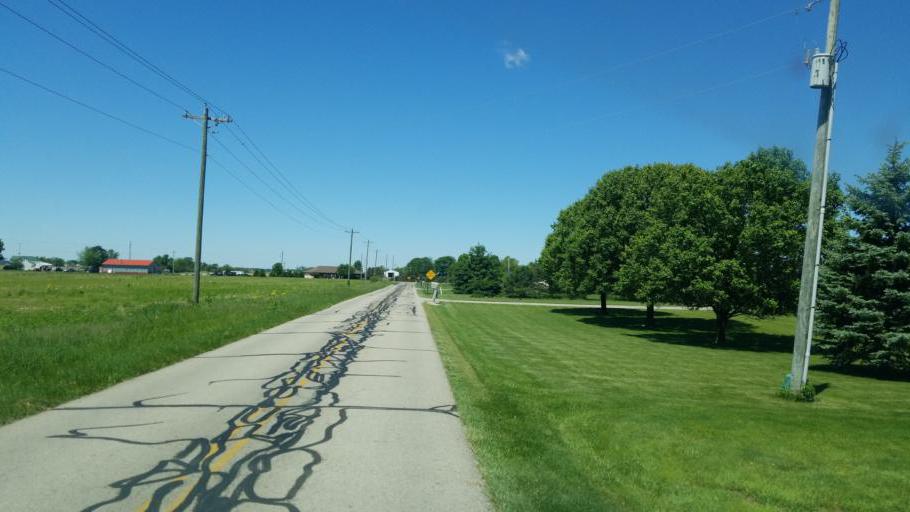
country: US
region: Ohio
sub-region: Shelby County
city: Anna
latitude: 40.3802
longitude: -84.2366
